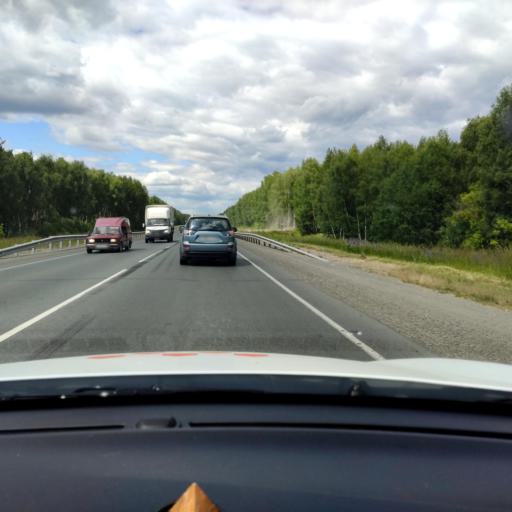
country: RU
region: Mariy-El
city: Pomary
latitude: 55.9358
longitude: 48.3722
